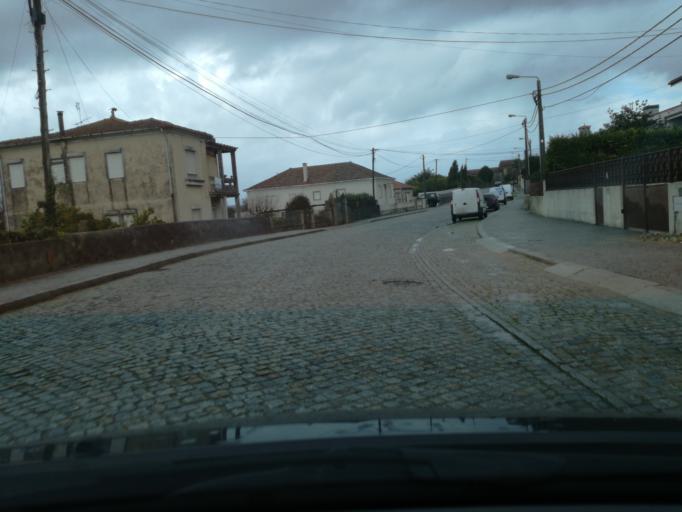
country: PT
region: Porto
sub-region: Valongo
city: Alfena
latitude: 41.2566
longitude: -8.5467
